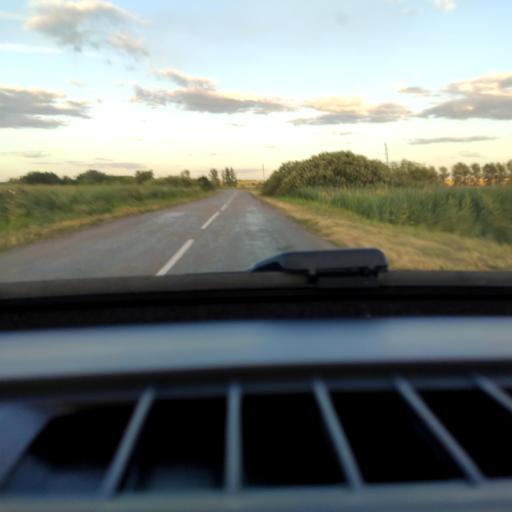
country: RU
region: Voronezj
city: Orlovo
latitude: 51.6462
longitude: 39.7246
